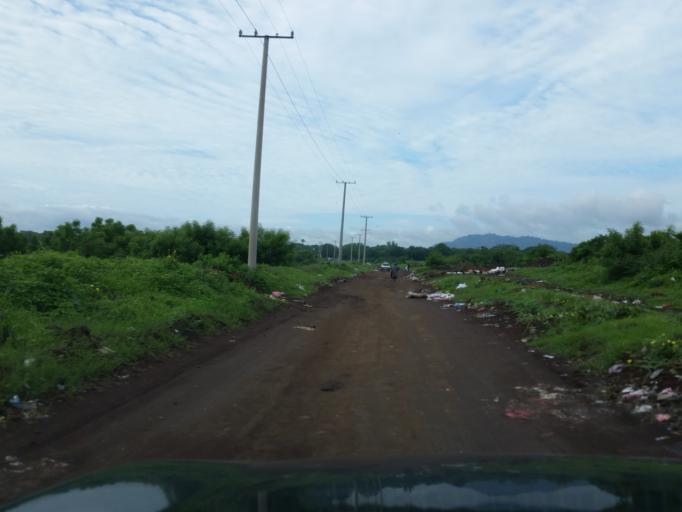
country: NI
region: Managua
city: Managua
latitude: 12.1021
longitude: -86.2057
